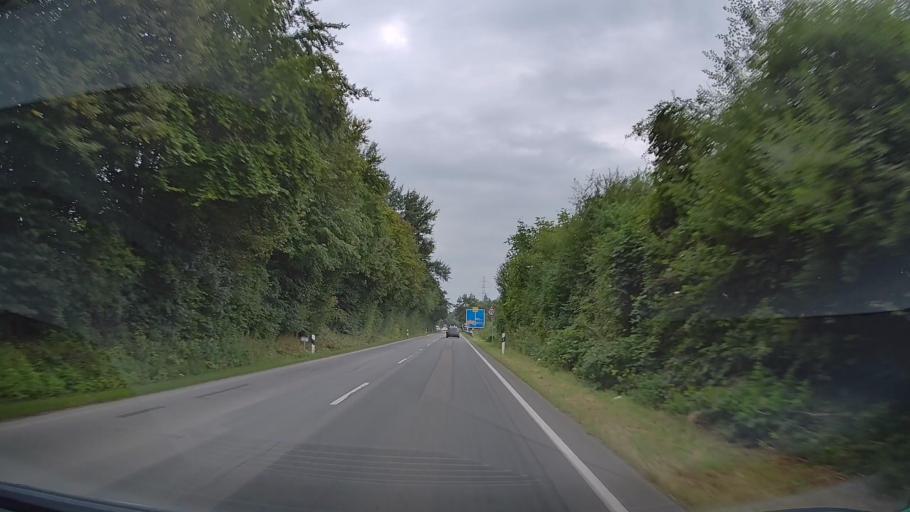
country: DE
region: Schleswig-Holstein
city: Scharbeutz
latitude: 54.0557
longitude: 10.7434
